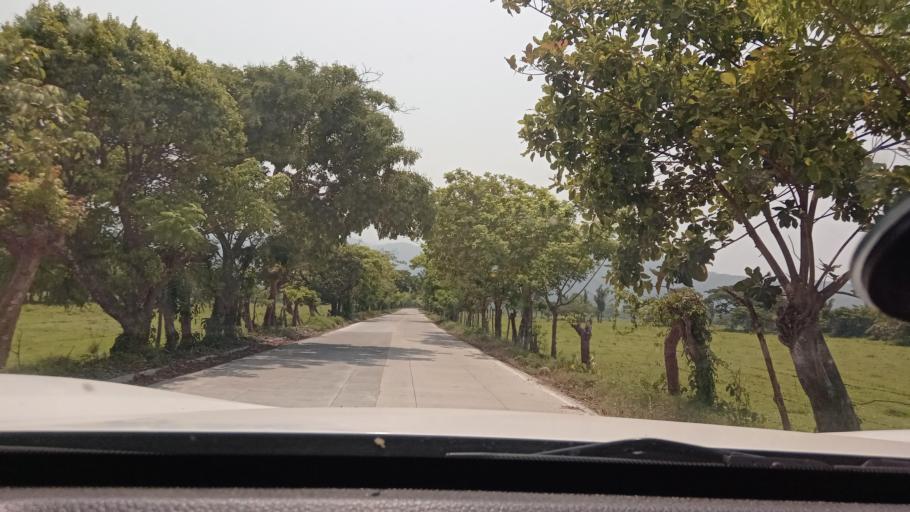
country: MX
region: Veracruz
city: Catemaco
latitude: 18.5622
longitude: -95.0431
